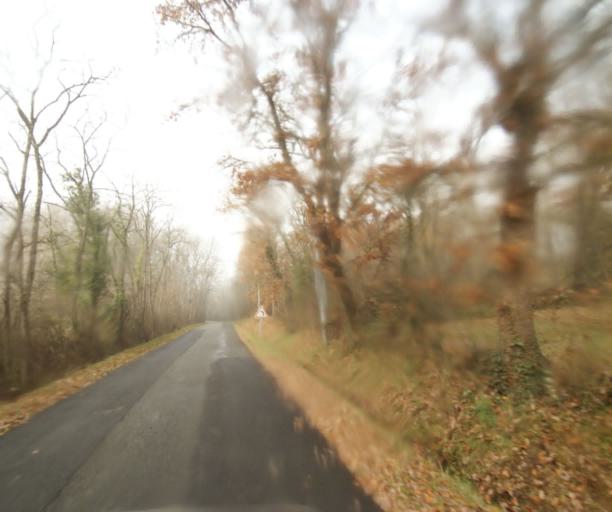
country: FR
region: Midi-Pyrenees
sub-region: Departement de la Haute-Garonne
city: Villaudric
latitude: 43.8203
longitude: 1.4586
